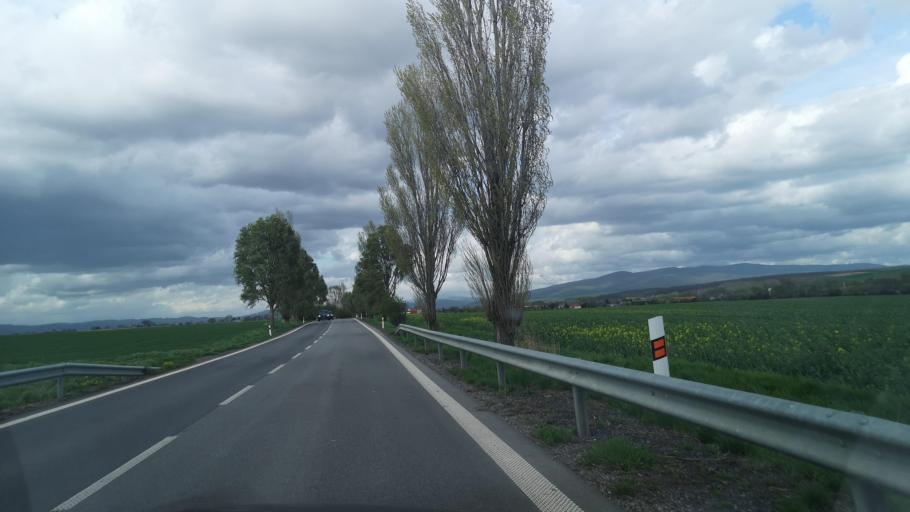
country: SK
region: Nitriansky
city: Zlate Moravce
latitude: 48.3212
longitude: 18.3449
